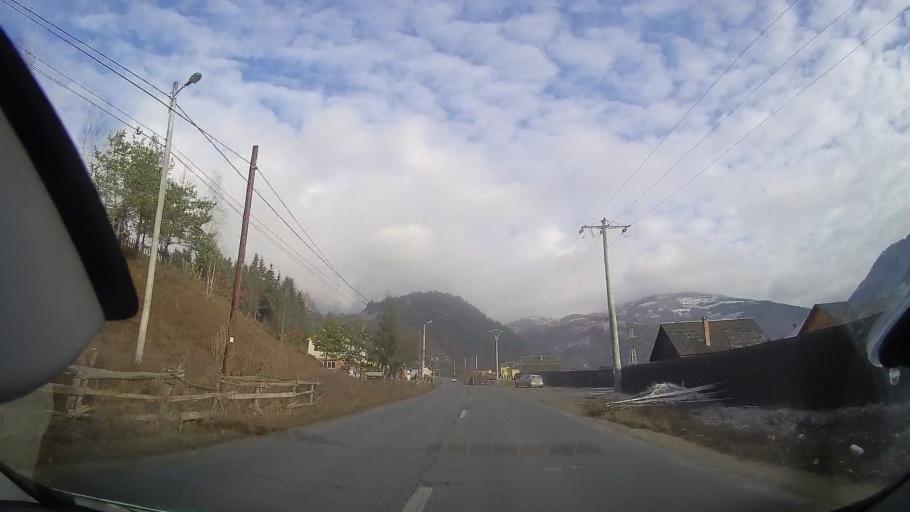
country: RO
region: Alba
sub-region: Comuna Bistra
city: Bistra
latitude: 46.3765
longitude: 23.1167
